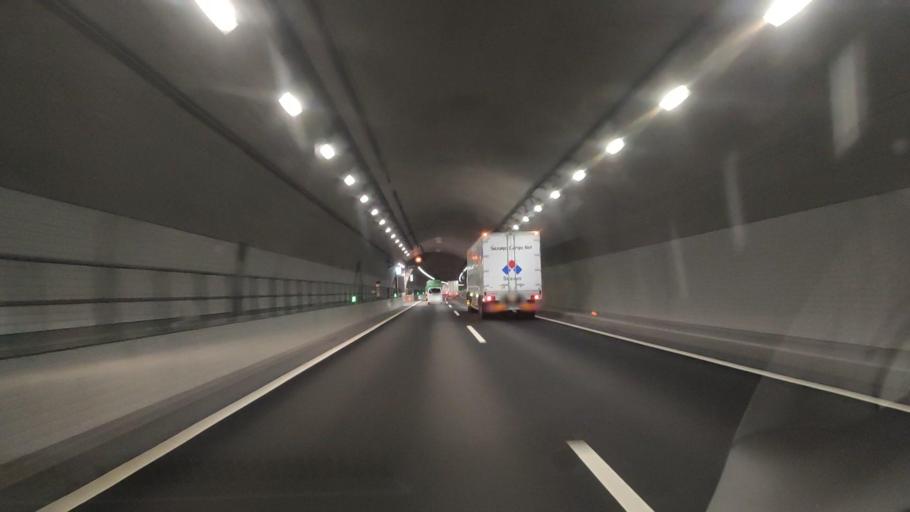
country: JP
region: Tokyo
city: Hachioji
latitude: 35.5691
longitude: 139.3052
